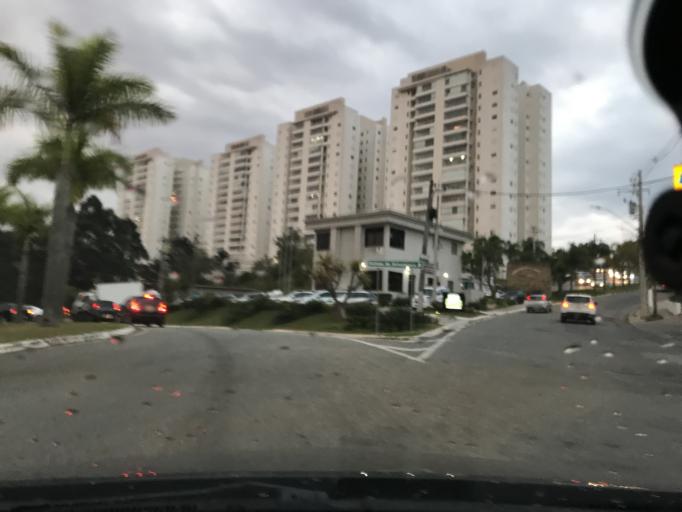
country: BR
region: Sao Paulo
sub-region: Carapicuiba
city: Carapicuiba
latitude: -23.4784
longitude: -46.8320
